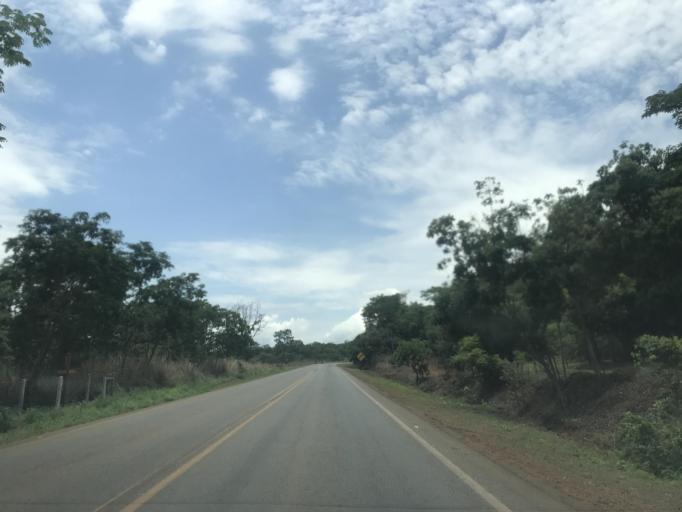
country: BR
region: Goias
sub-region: Vianopolis
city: Vianopolis
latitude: -16.7175
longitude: -48.4052
